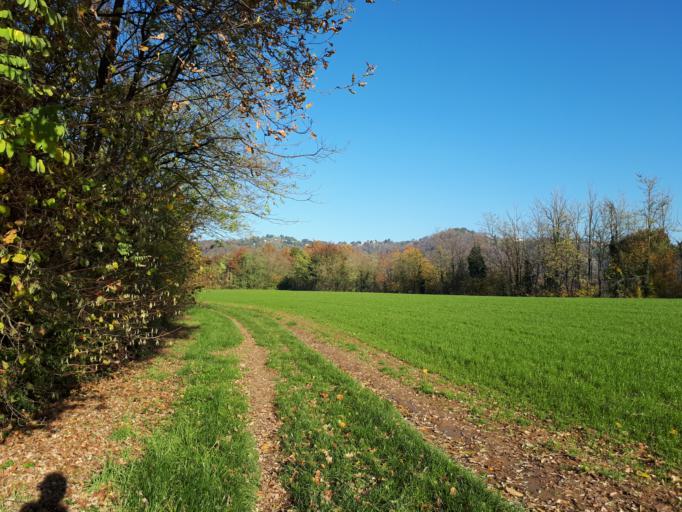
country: IT
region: Lombardy
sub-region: Provincia di Lecco
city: Maresso
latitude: 45.6949
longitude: 9.3613
